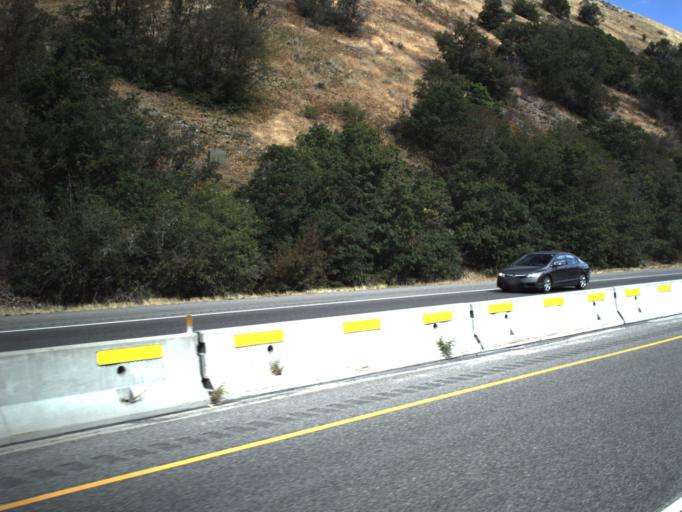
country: US
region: Utah
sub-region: Cache County
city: Wellsville
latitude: 41.6036
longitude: -111.9589
